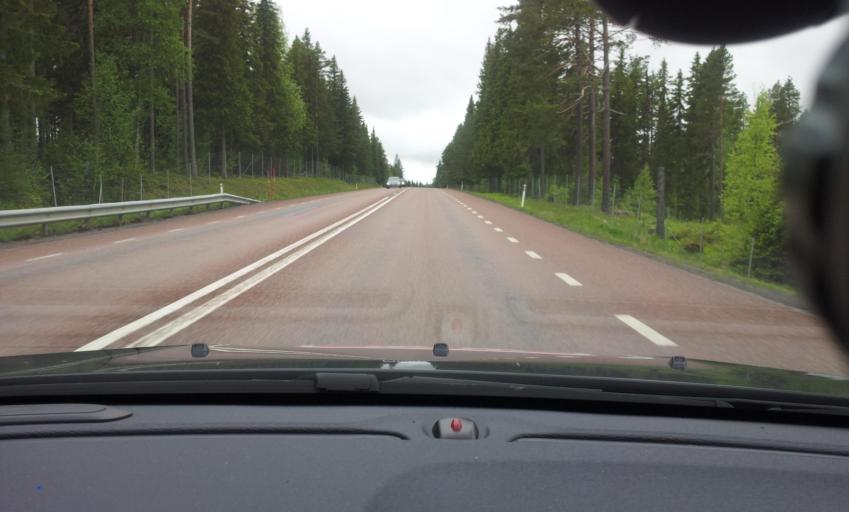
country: SE
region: Jaemtland
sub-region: Krokoms Kommun
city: Krokom
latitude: 63.3261
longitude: 14.3745
